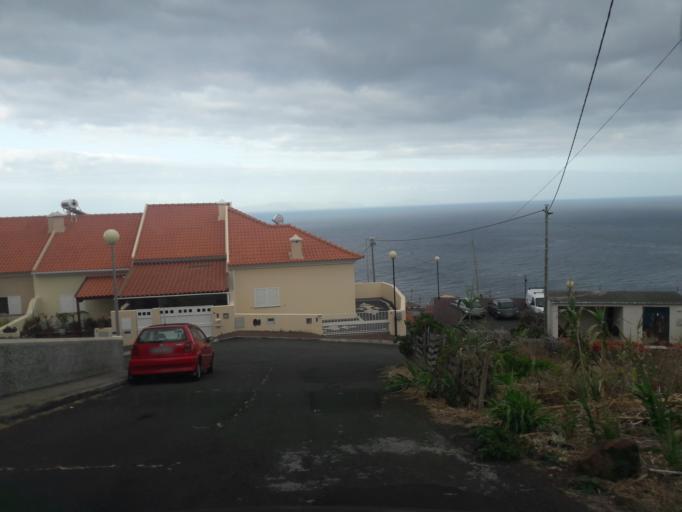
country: PT
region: Madeira
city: Canico
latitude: 32.6434
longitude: -16.8432
